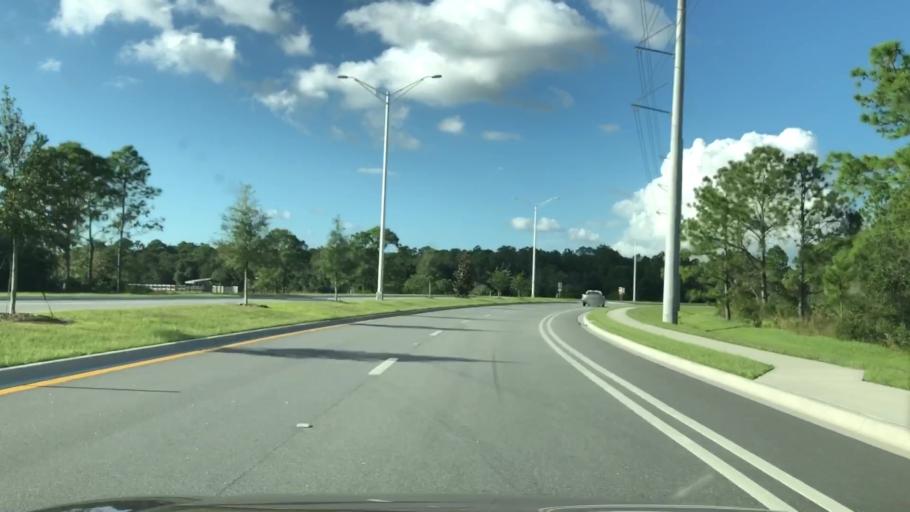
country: US
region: Florida
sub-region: Sarasota County
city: Fruitville
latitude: 27.3531
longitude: -82.3862
